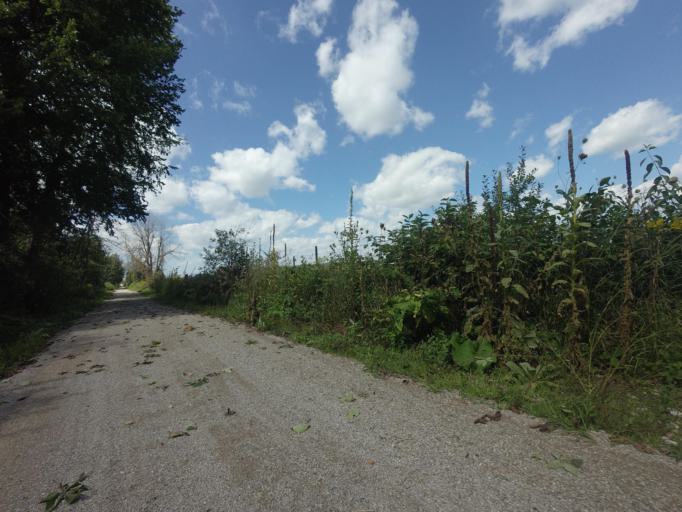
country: CA
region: Ontario
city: Huron East
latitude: 43.6391
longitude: -81.1998
